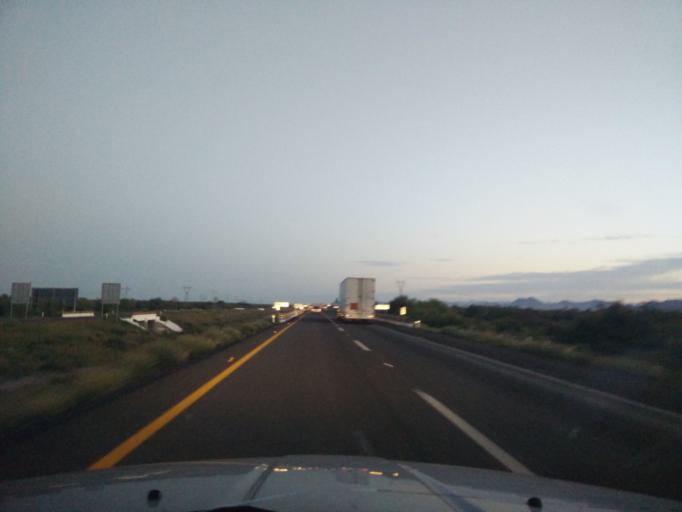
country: MX
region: Sonora
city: Heroica Guaymas
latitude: 28.0597
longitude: -110.9471
